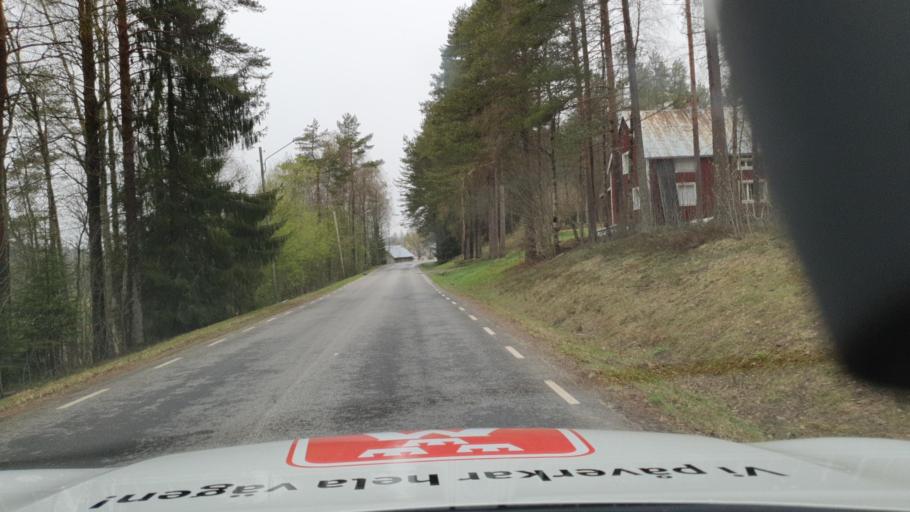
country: SE
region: Vaesterbotten
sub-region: Nordmalings Kommun
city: Nordmaling
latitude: 63.7064
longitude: 19.5967
